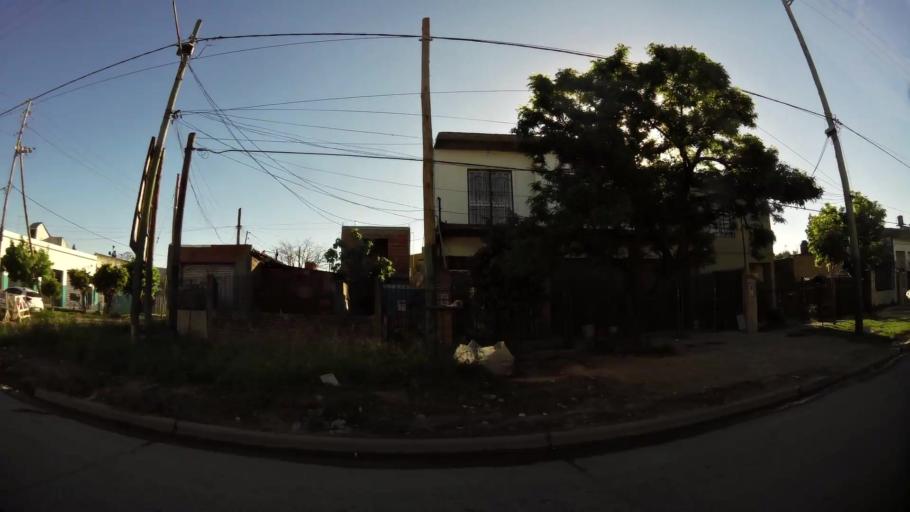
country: AR
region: Buenos Aires
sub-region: Partido de Almirante Brown
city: Adrogue
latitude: -34.7638
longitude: -58.3298
